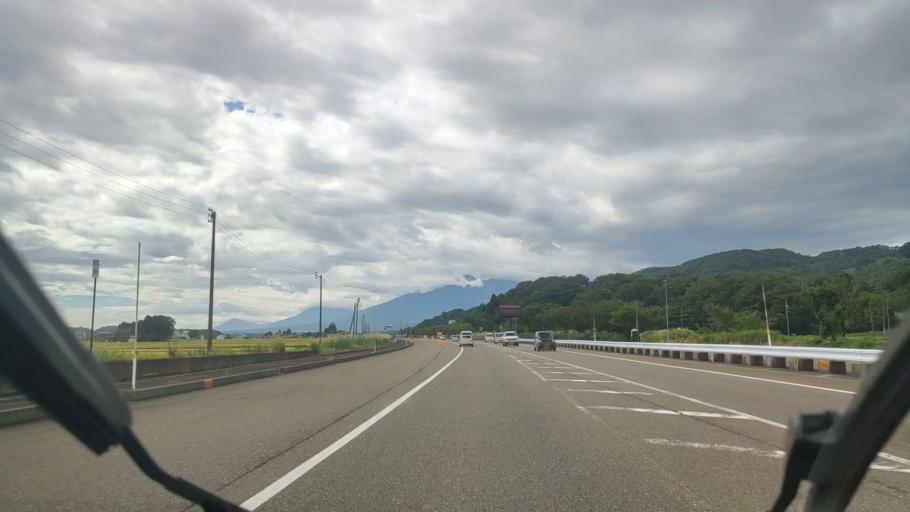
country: JP
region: Niigata
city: Arai
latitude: 37.0453
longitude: 138.2397
